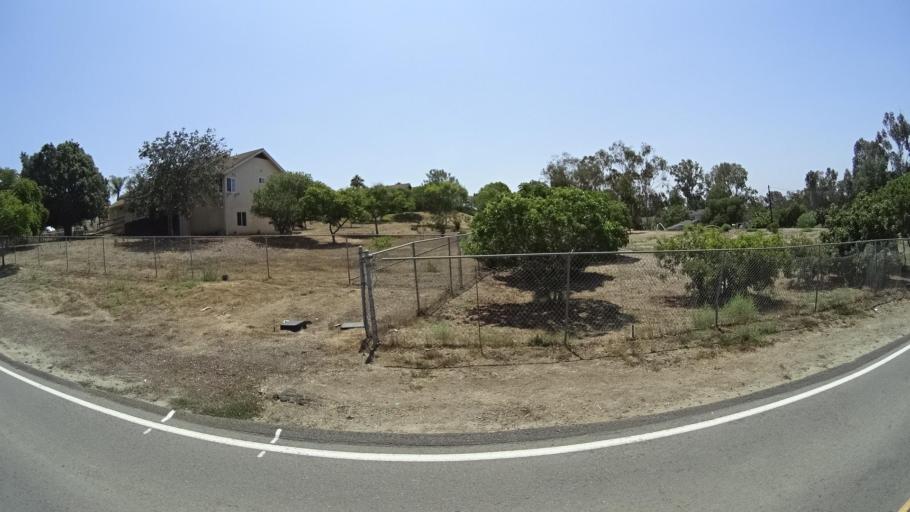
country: US
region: California
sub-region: San Diego County
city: Vista
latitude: 33.1816
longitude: -117.2660
